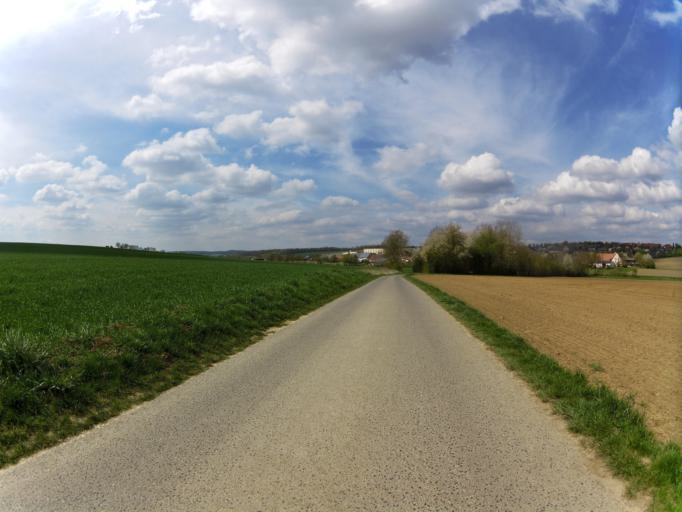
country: DE
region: Bavaria
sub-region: Regierungsbezirk Unterfranken
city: Sulzdorf
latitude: 49.6468
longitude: 9.9097
